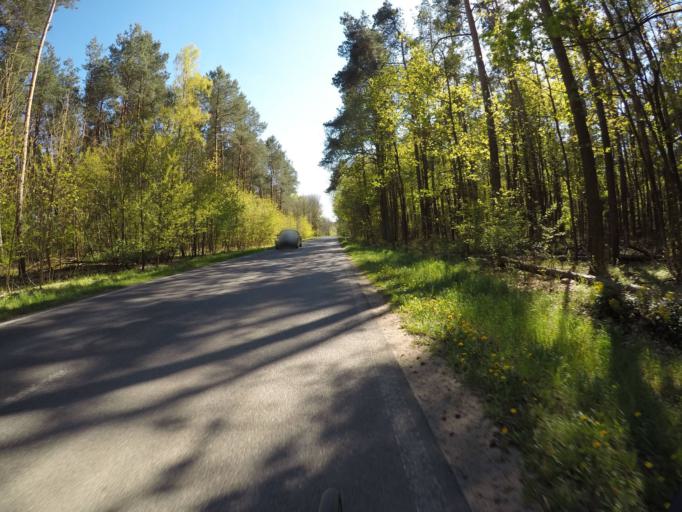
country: DE
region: Brandenburg
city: Rehfelde
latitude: 52.5494
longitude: 13.9399
